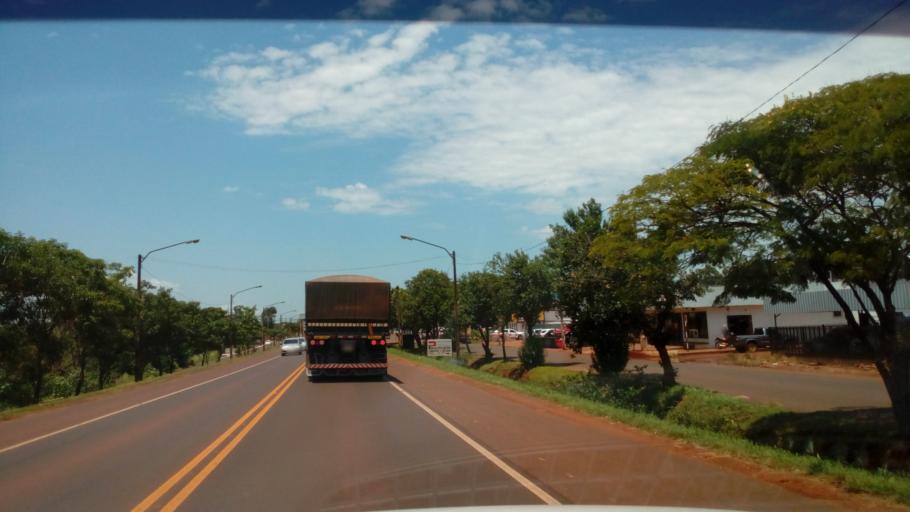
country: PY
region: Alto Parana
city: Santa Rita
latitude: -25.8044
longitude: -55.0963
